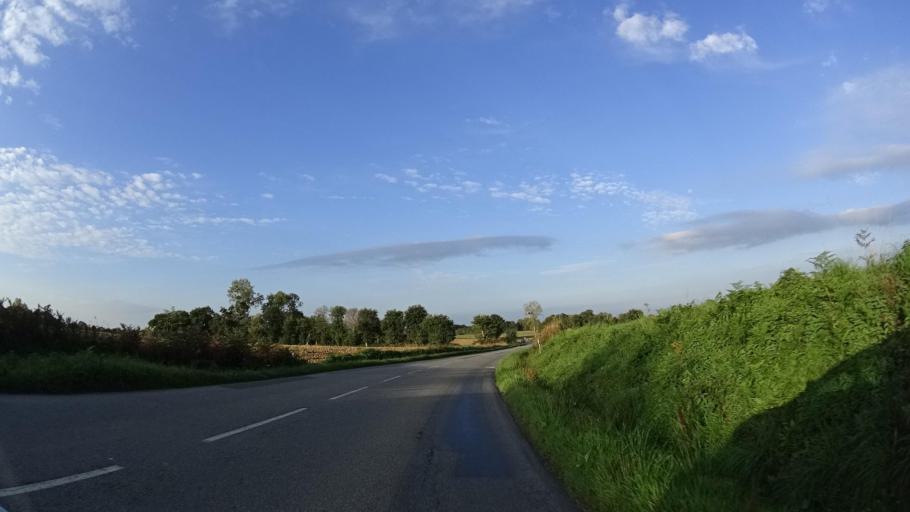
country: FR
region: Brittany
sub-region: Departement d'Ille-et-Vilaine
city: Irodouer
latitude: 48.2882
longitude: -1.9643
